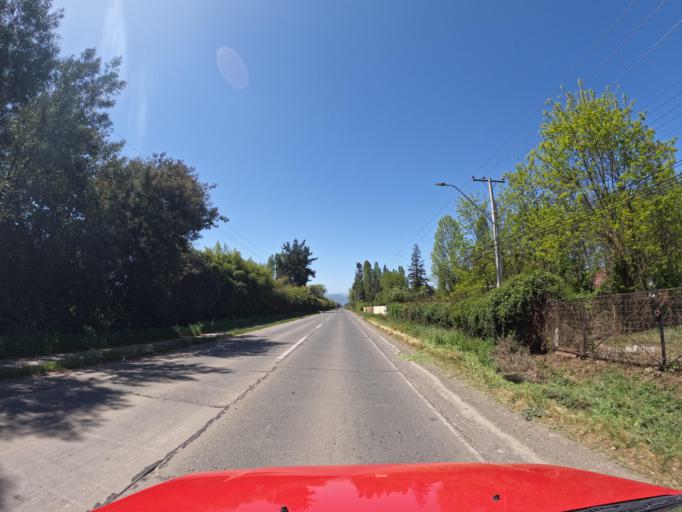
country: CL
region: Maule
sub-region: Provincia de Linares
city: Linares
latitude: -35.8340
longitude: -71.5417
